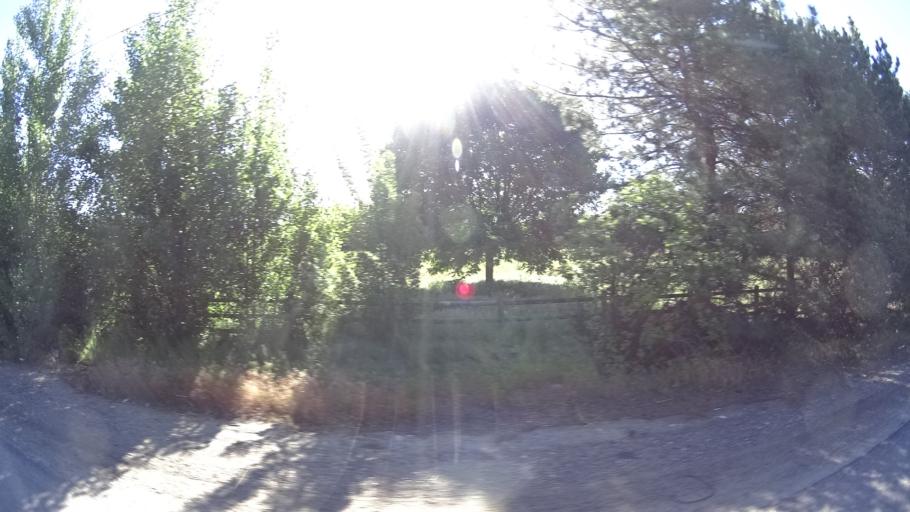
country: US
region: Idaho
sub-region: Ada County
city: Eagle
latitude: 43.6755
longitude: -116.4136
